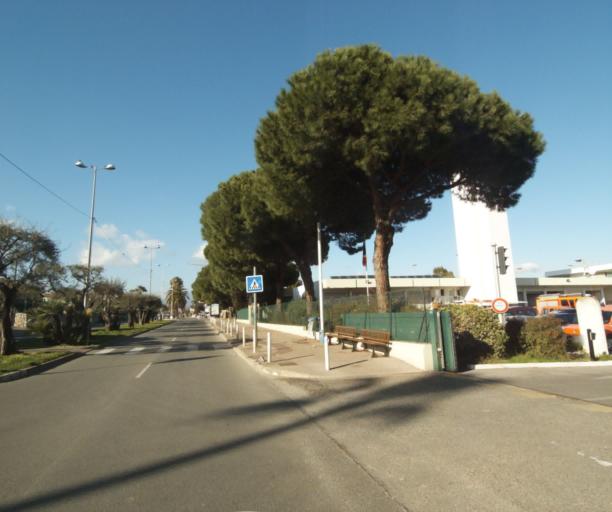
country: FR
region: Provence-Alpes-Cote d'Azur
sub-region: Departement des Alpes-Maritimes
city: Antibes
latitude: 43.5908
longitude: 7.1170
